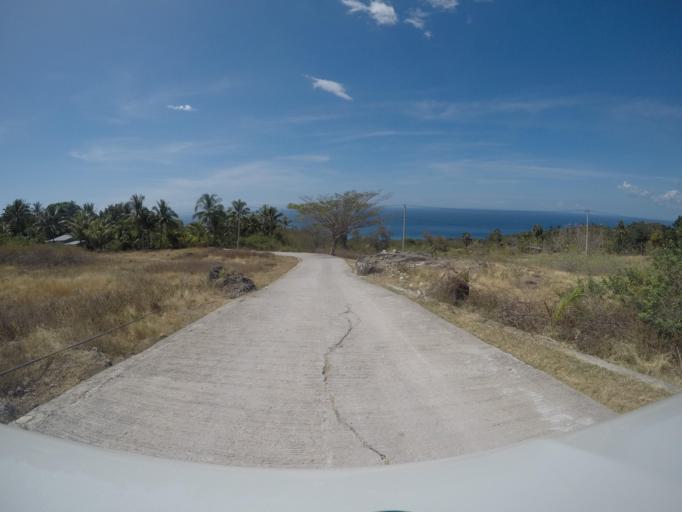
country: TL
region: Baucau
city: Baucau
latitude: -8.4514
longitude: 126.4487
